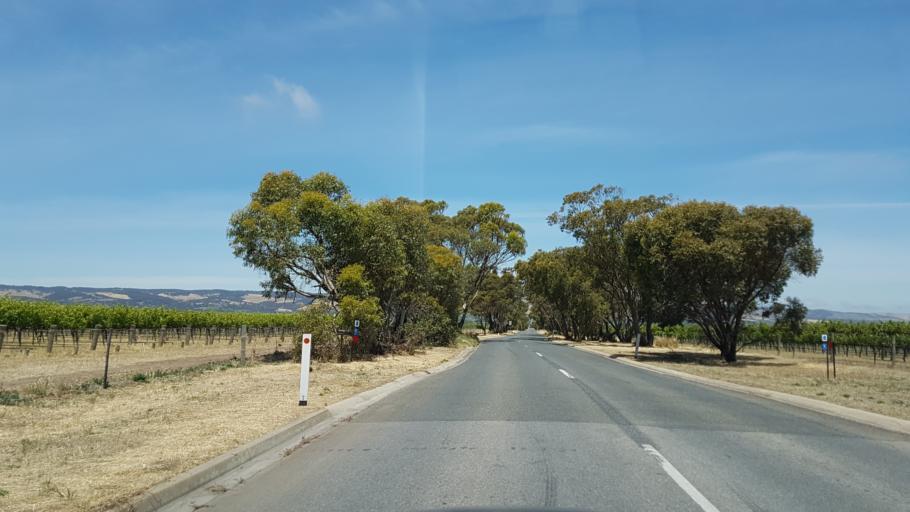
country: AU
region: South Australia
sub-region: Onkaparinga
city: McLaren Vale
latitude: -35.2314
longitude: 138.5190
